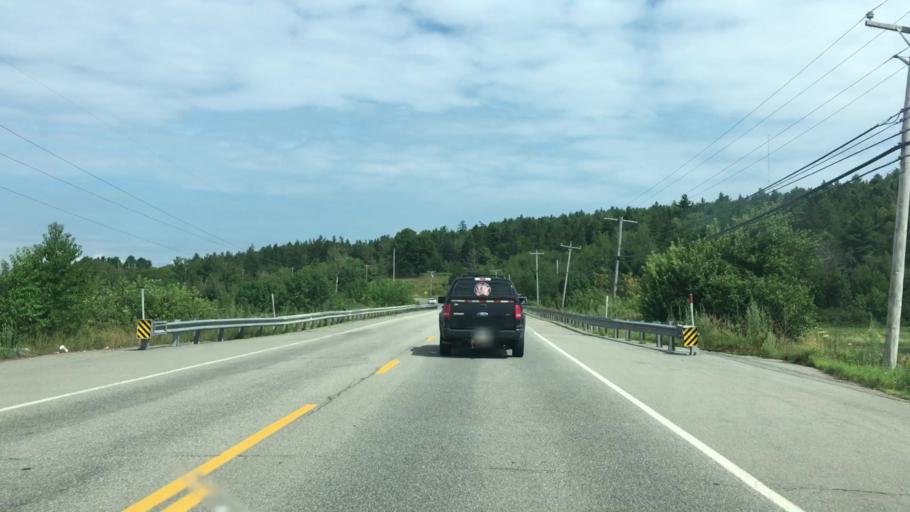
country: US
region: Maine
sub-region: Washington County
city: Calais
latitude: 45.1512
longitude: -67.2856
